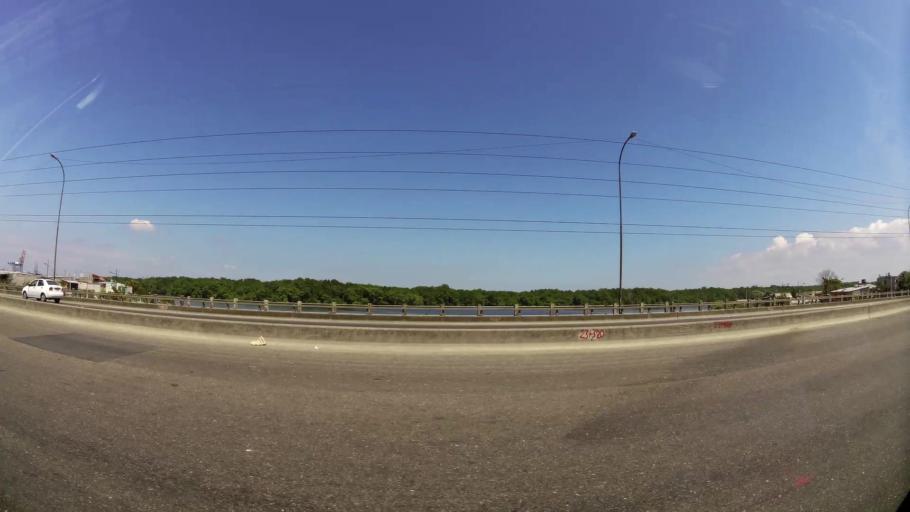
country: EC
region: Guayas
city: Guayaquil
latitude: -2.2341
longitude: -79.9388
